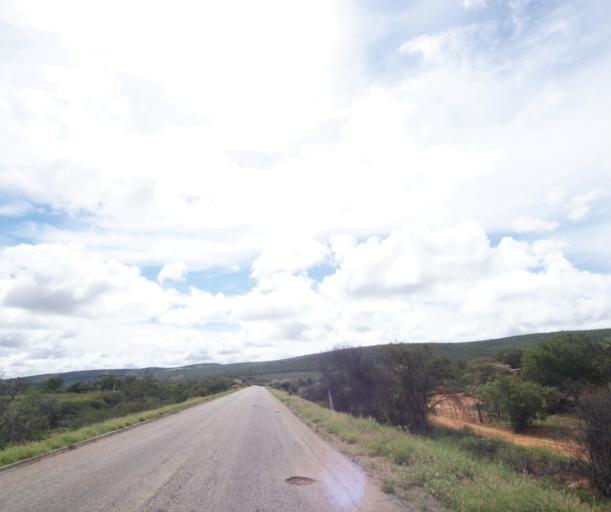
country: BR
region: Bahia
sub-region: Brumado
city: Brumado
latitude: -14.1993
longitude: -41.6109
